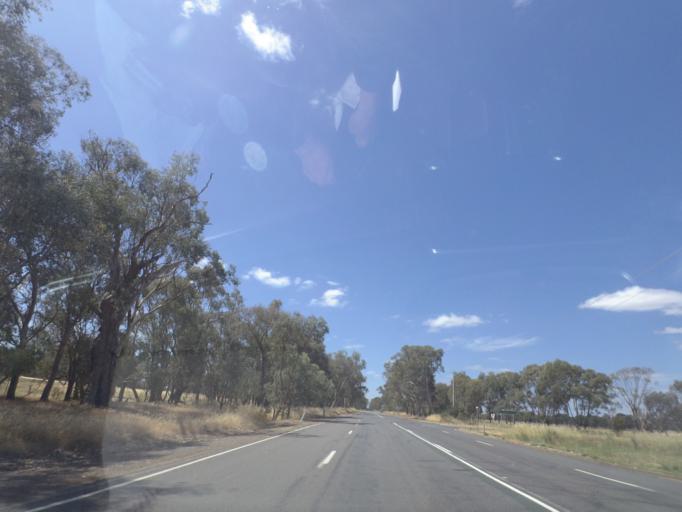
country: AU
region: Victoria
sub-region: Wangaratta
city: Wangaratta
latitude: -36.4263
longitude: 146.2570
